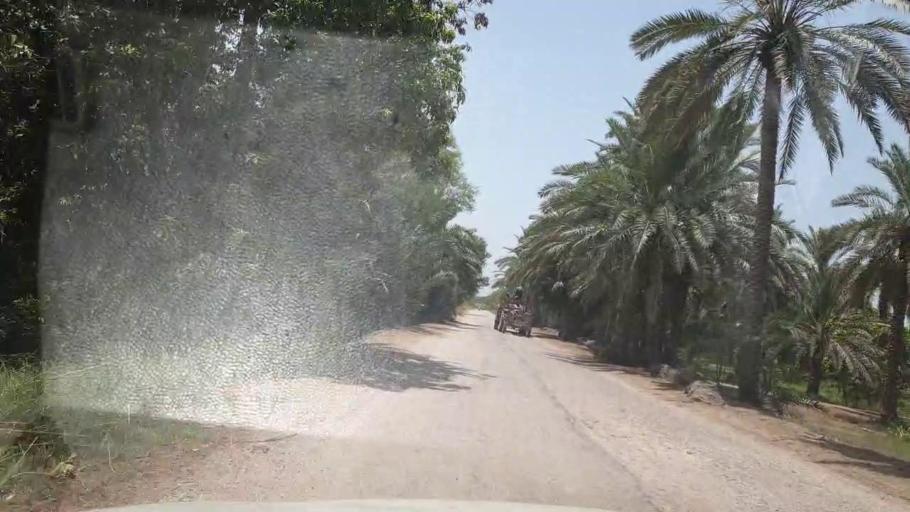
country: PK
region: Sindh
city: Bozdar
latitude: 27.1888
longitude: 68.5955
